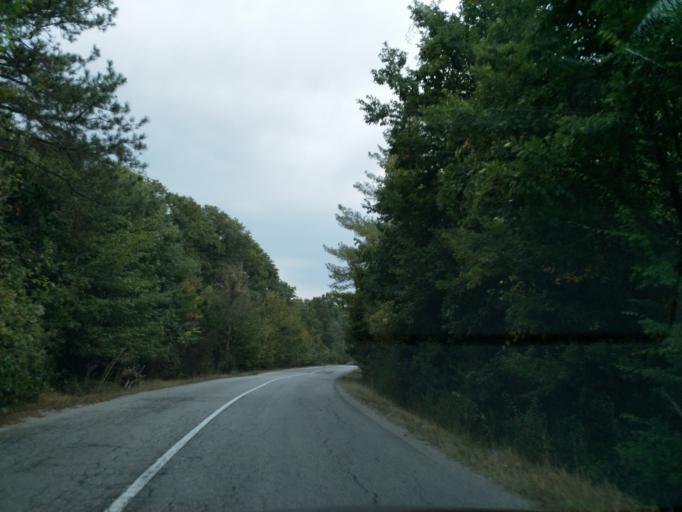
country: RS
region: Central Serbia
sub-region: Pomoravski Okrug
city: Jagodina
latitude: 44.0283
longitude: 21.1962
